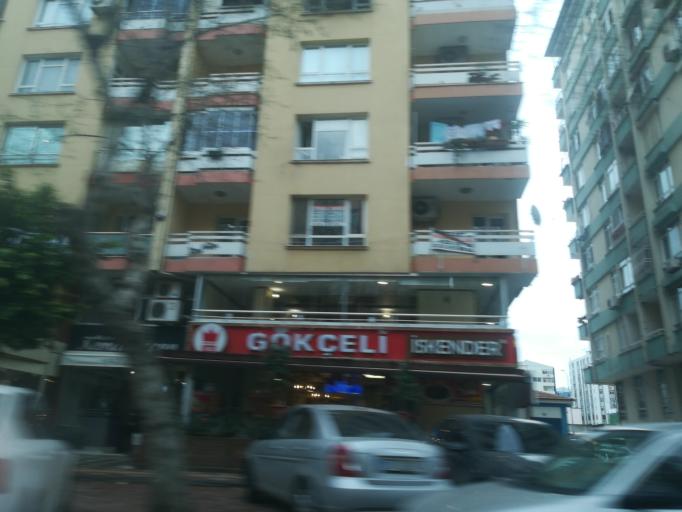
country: TR
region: Adana
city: Adana
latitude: 36.9934
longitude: 35.3228
